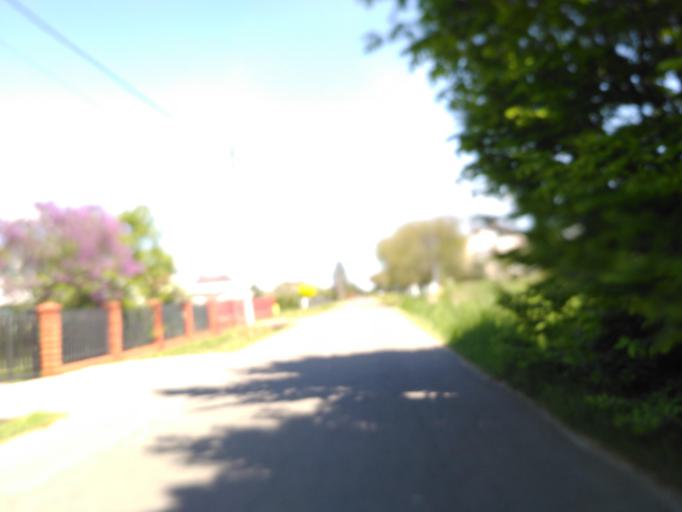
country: PL
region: Subcarpathian Voivodeship
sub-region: Powiat krosnienski
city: Jedlicze
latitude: 49.7009
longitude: 21.6833
